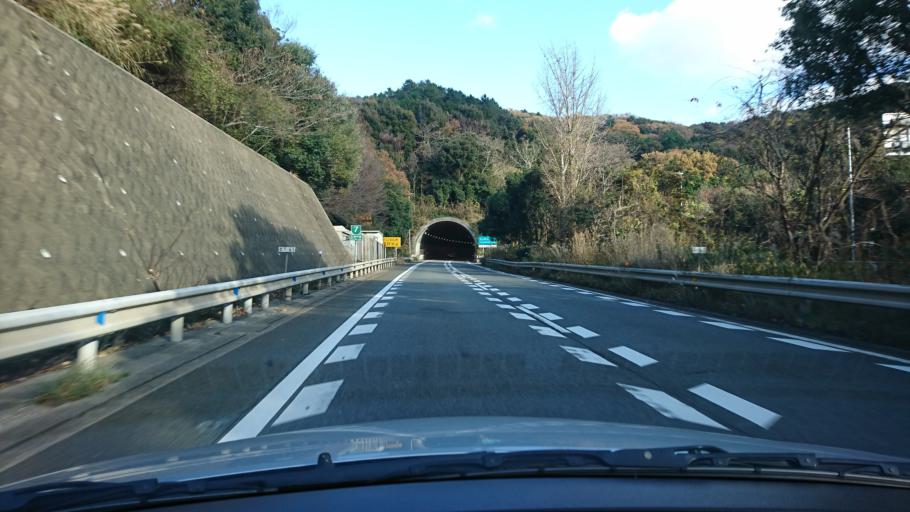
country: JP
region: Hyogo
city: Akashi
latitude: 34.7009
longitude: 135.0670
